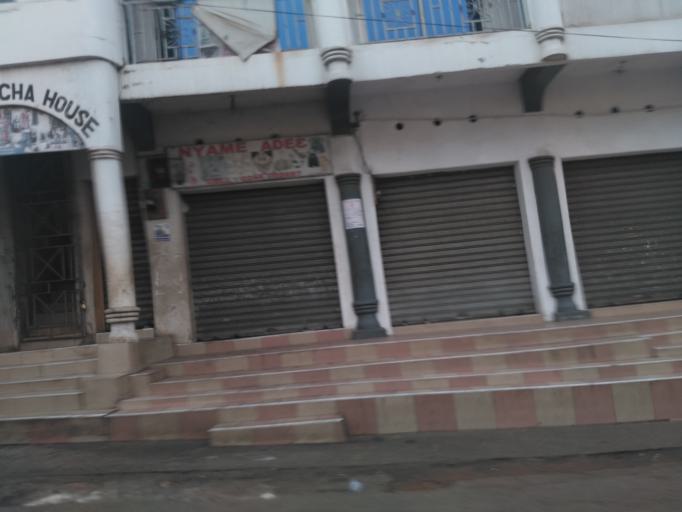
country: GH
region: Ashanti
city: Kumasi
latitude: 6.7007
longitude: -1.6176
